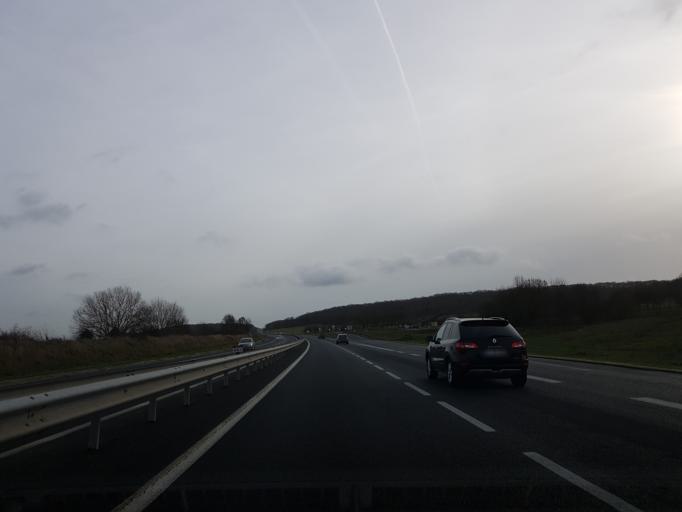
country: FR
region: Bourgogne
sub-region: Departement de l'Yonne
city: Soucy
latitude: 48.2480
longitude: 3.3458
